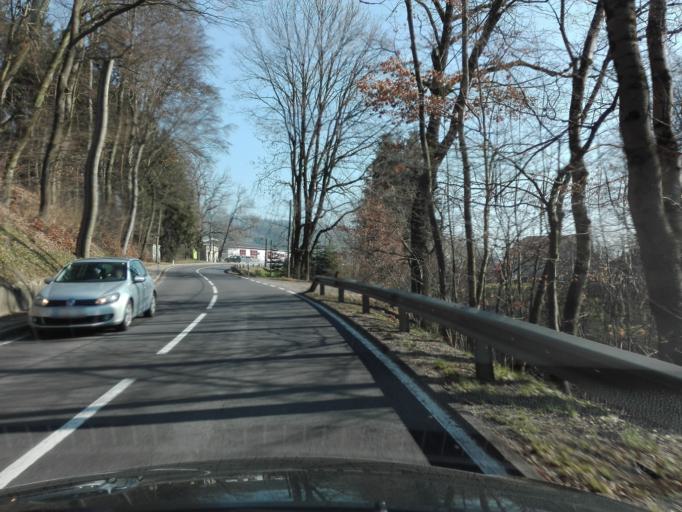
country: AT
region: Upper Austria
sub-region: Politischer Bezirk Urfahr-Umgebung
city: Altenberg bei Linz
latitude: 48.3359
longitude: 14.3547
